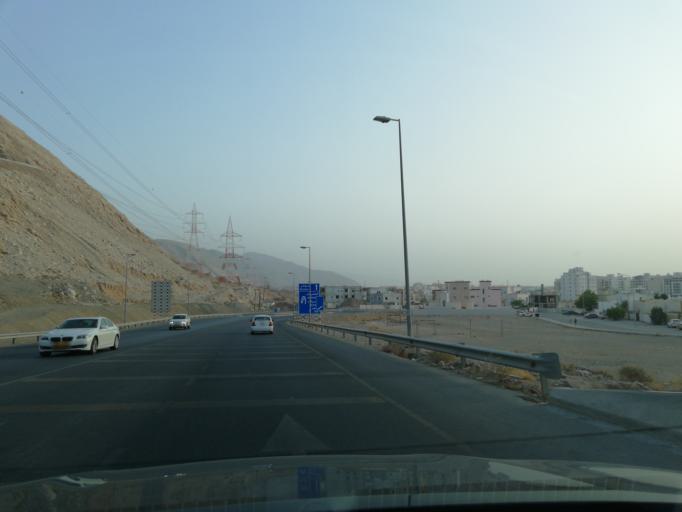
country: OM
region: Muhafazat Masqat
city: Bawshar
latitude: 23.5650
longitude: 58.4266
